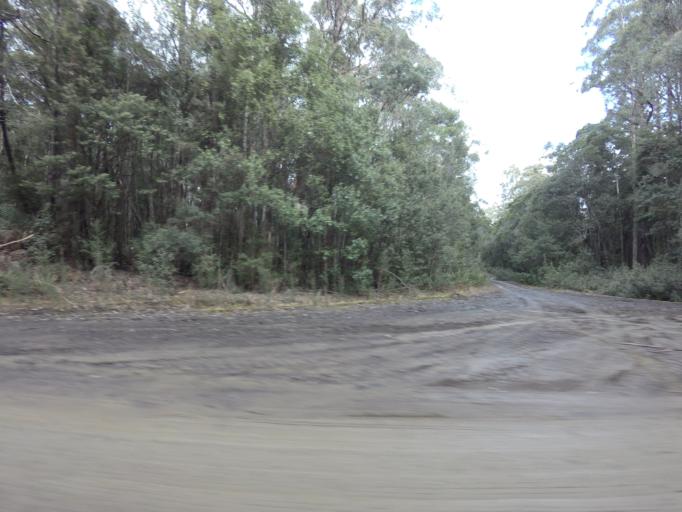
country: AU
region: Tasmania
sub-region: Huon Valley
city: Geeveston
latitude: -43.4014
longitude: 146.8619
